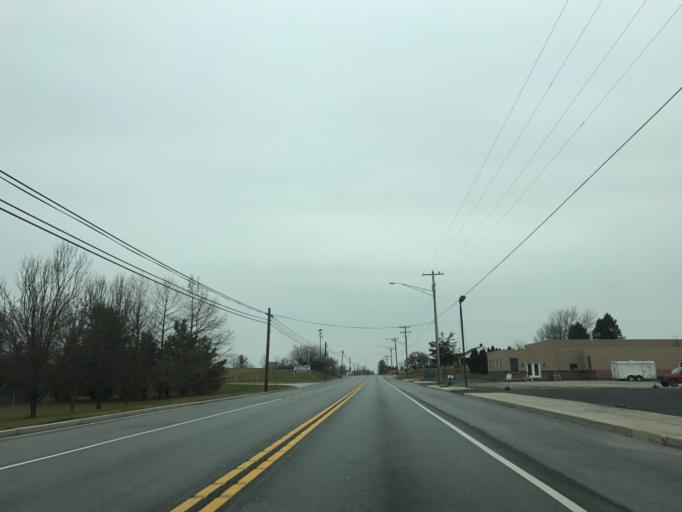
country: US
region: Maryland
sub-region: Carroll County
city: Taneytown
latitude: 39.6645
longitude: -77.1840
